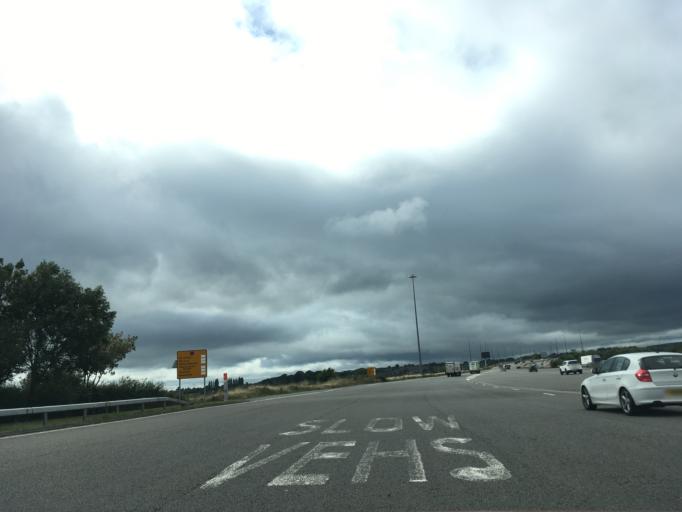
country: GB
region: Wales
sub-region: Monmouthshire
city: Rogiet
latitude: 51.5807
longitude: -2.7861
